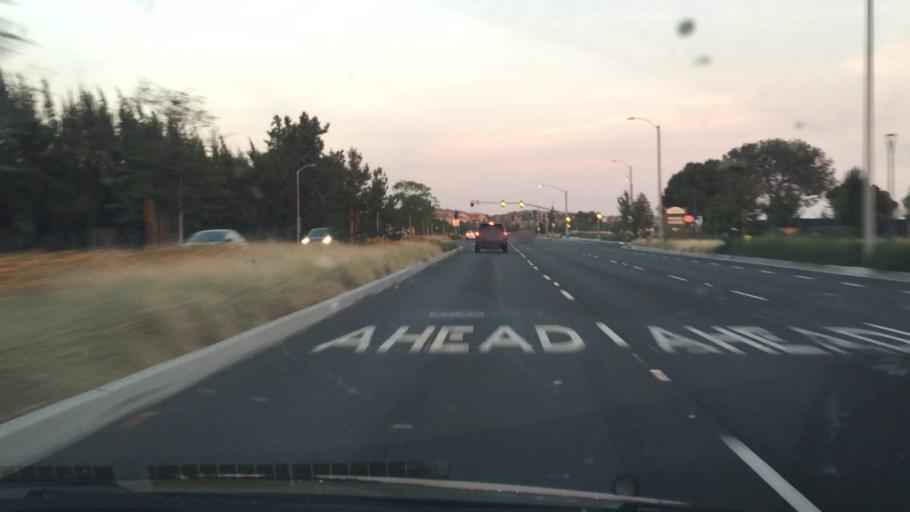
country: US
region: California
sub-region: Orange County
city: Lake Forest
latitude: 33.6861
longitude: -117.7205
